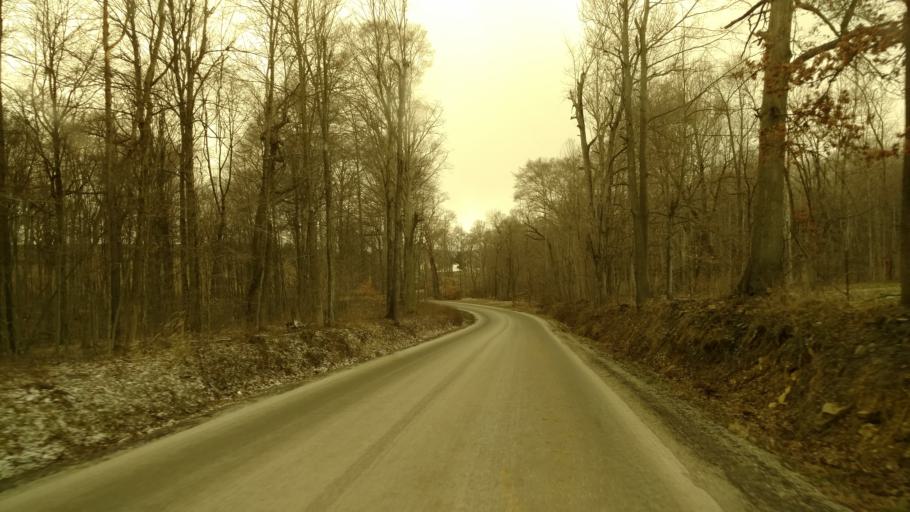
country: US
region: Ohio
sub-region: Tuscarawas County
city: Sugarcreek
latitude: 40.4462
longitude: -81.7739
